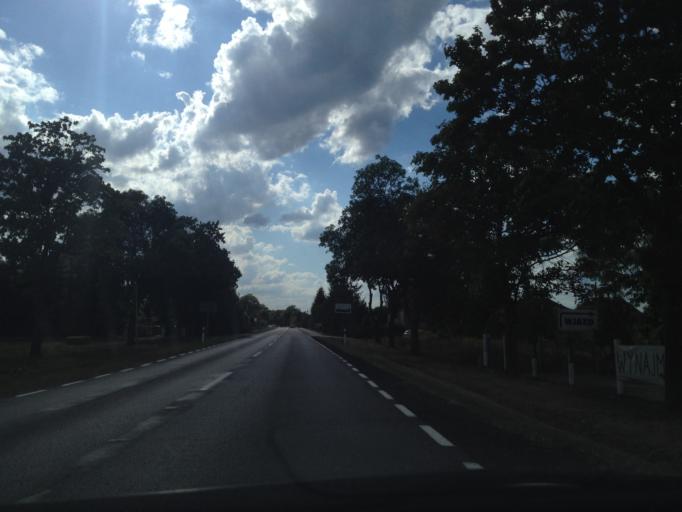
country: PL
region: Lubusz
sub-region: Powiat zarski
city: Sieniawa Zarska
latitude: 51.6307
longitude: 15.0788
